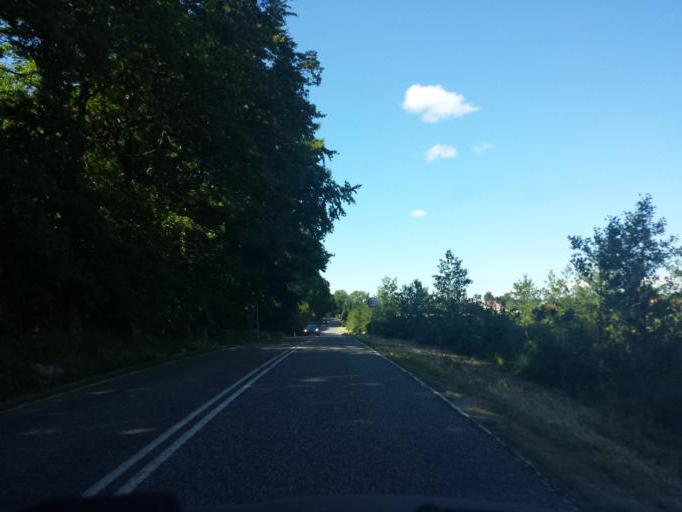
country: DK
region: Capital Region
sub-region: Egedal Kommune
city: Ganlose
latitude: 55.8099
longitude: 12.2617
